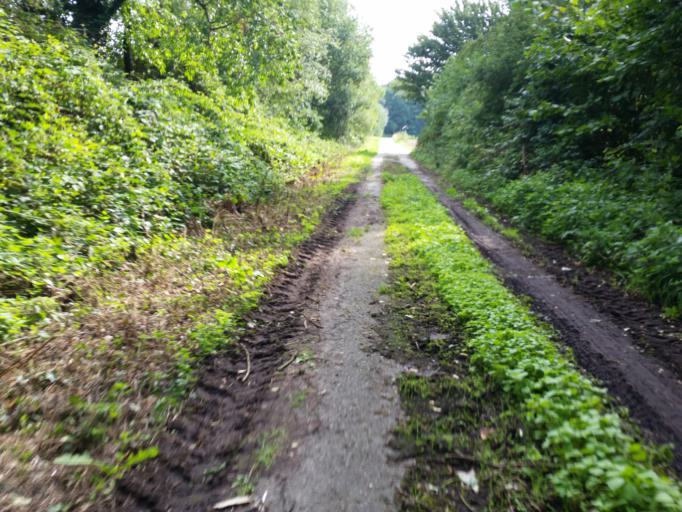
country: BE
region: Flanders
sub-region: Provincie Vlaams-Brabant
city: Zemst
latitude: 50.9552
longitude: 4.4864
